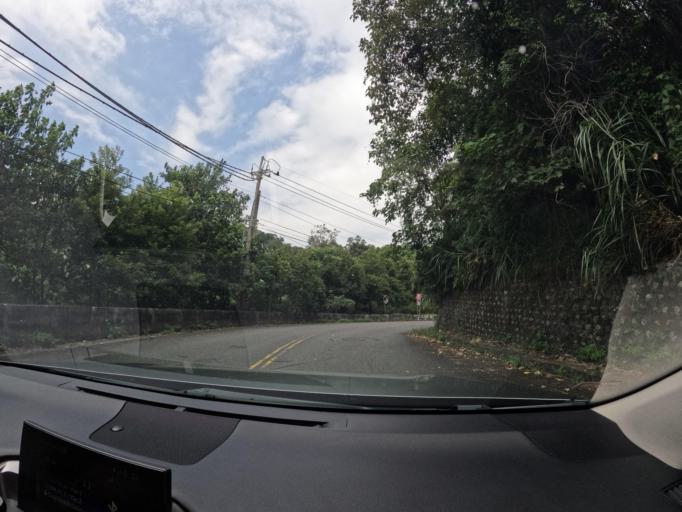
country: TW
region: Taiwan
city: Fengyuan
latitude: 24.3141
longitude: 120.8741
